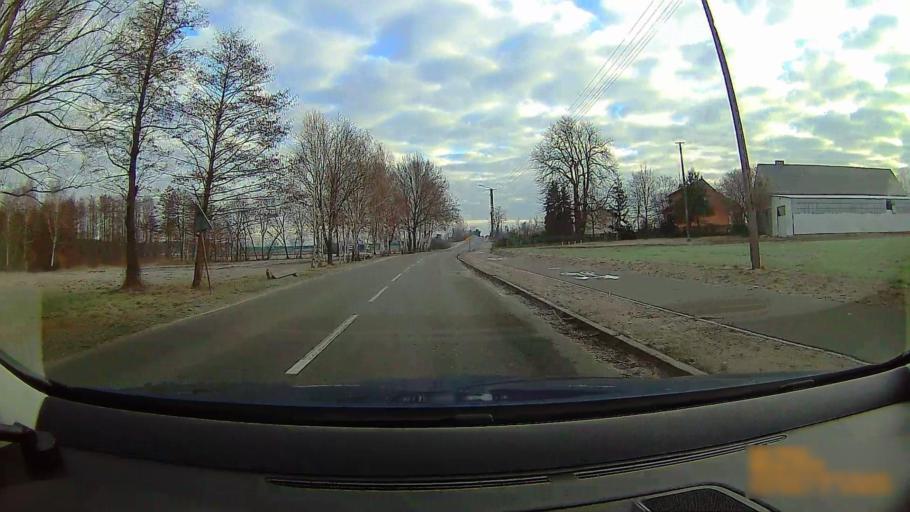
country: PL
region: Greater Poland Voivodeship
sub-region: Powiat koninski
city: Rzgow Pierwszy
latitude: 52.1805
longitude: 18.1012
